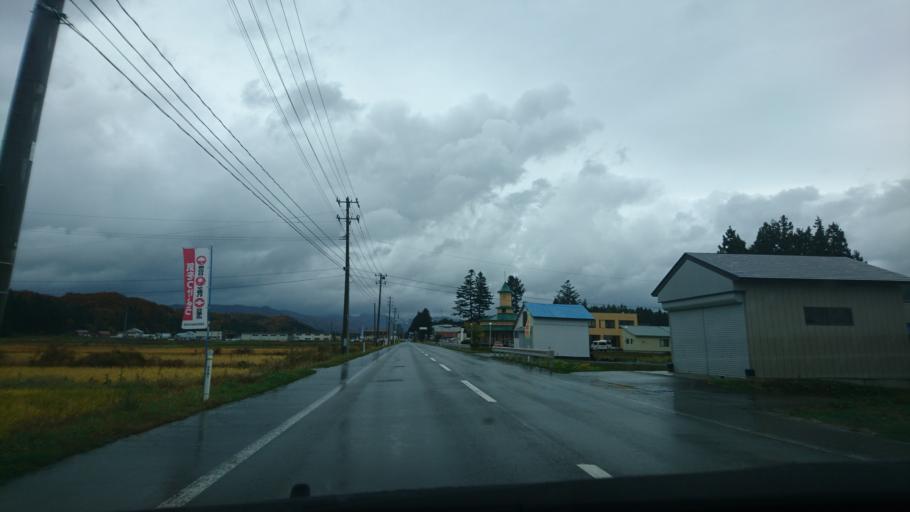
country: JP
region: Akita
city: Yokotemachi
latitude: 39.3698
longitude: 140.7609
